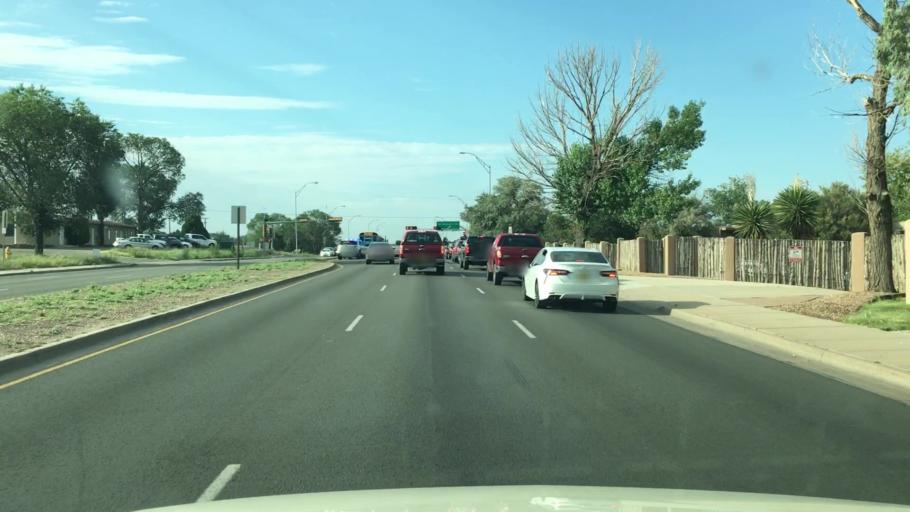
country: US
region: New Mexico
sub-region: Santa Fe County
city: Santa Fe
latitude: 35.6634
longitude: -105.9565
